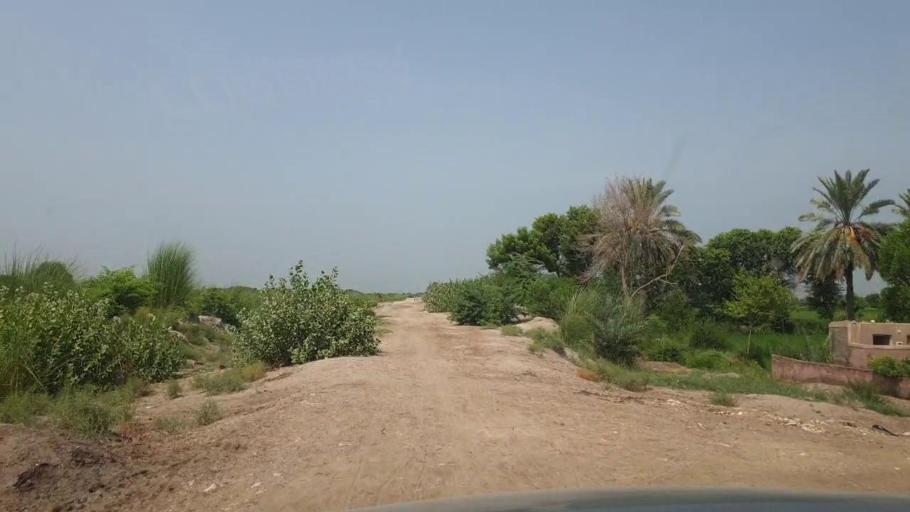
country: PK
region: Sindh
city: Madeji
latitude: 27.7846
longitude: 68.5349
